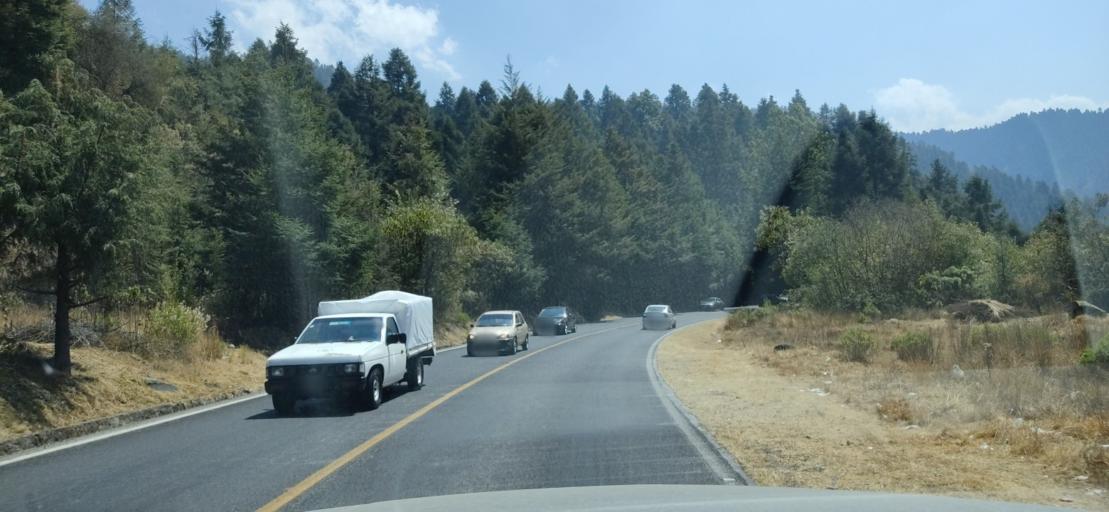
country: MX
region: Mexico
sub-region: Ocoyoacac
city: San Jeronimo Acazulco
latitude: 19.2507
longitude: -99.3728
